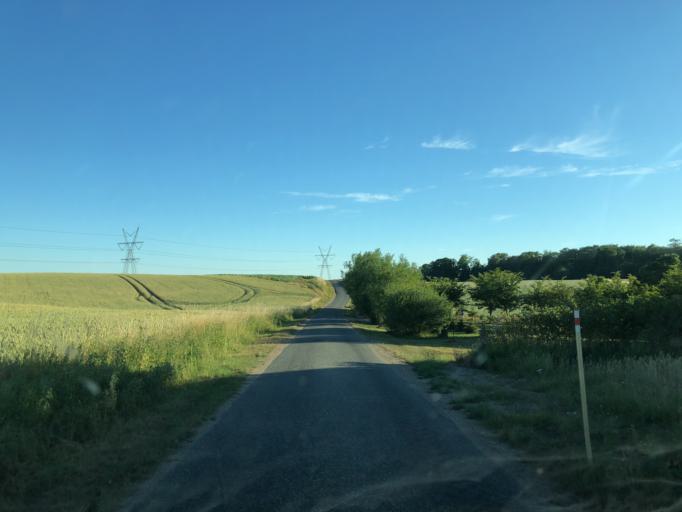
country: DK
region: Central Jutland
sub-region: Horsens Kommune
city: Horsens
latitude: 55.9153
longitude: 9.8800
